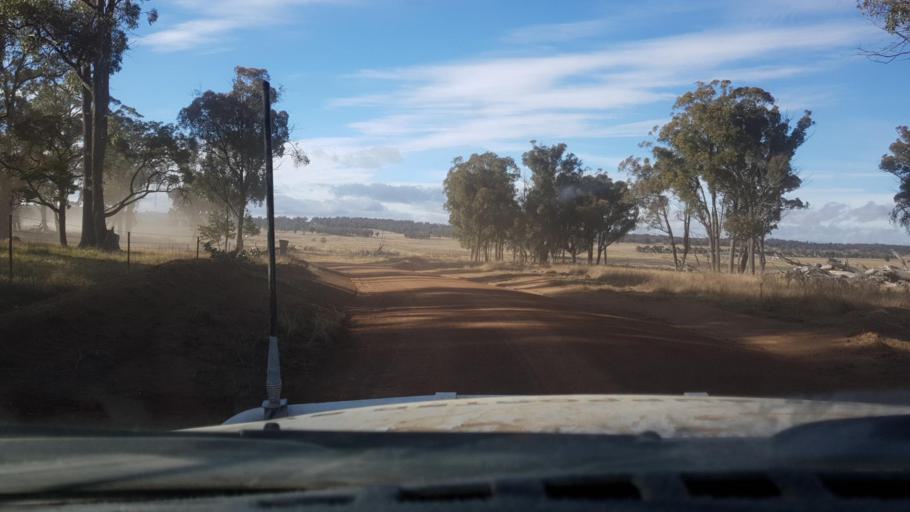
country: AU
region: New South Wales
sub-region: Armidale Dumaresq
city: Enmore
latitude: -30.7444
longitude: 151.6042
